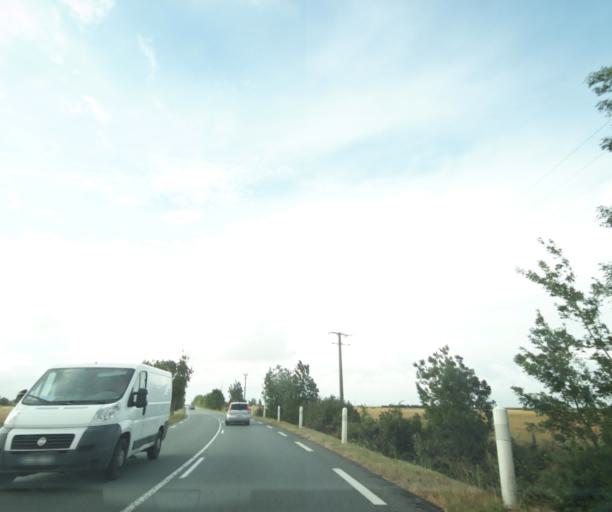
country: FR
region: Poitou-Charentes
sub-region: Departement de la Charente-Maritime
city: Charron
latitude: 46.2943
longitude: -1.0858
